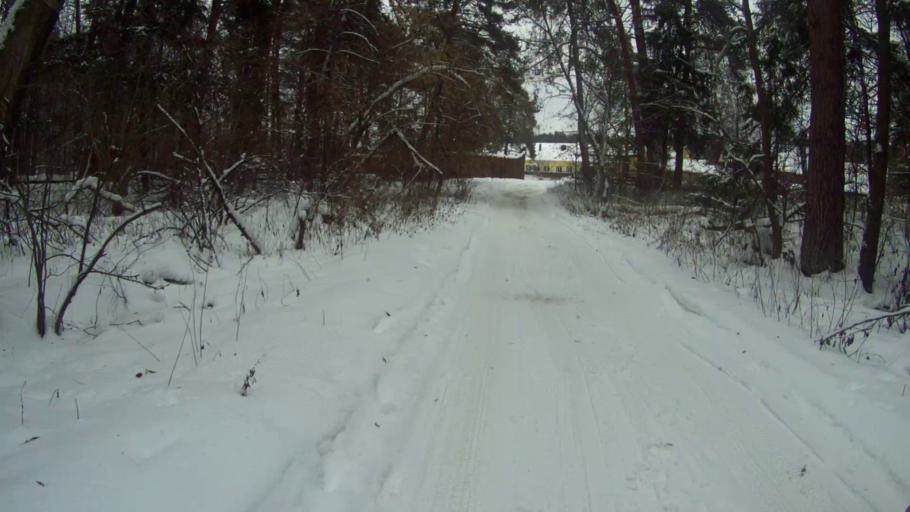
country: RU
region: Mordoviya
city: Sosnovka
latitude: 54.7125
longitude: 43.2223
